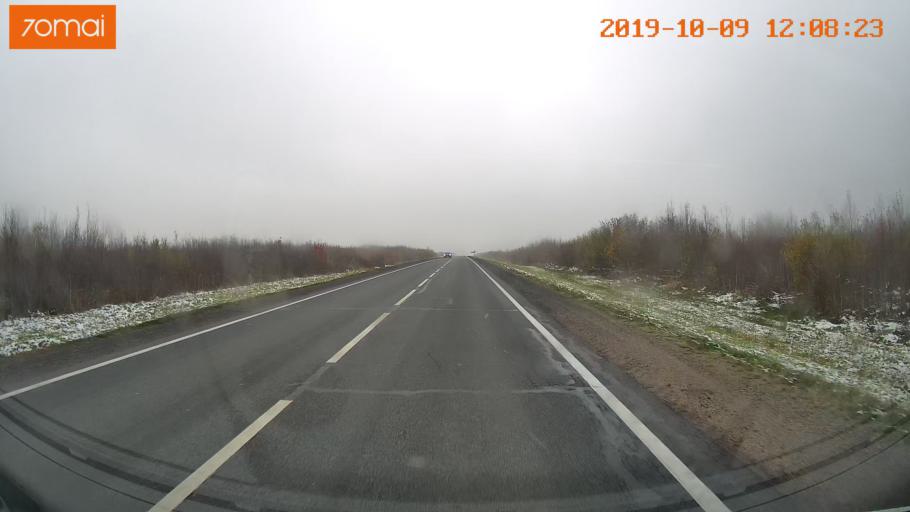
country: RU
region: Jaroslavl
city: Prechistoye
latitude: 58.5866
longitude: 40.3474
